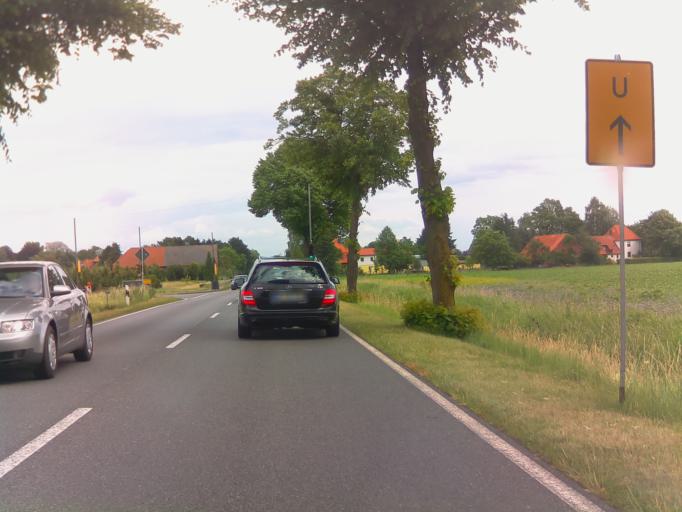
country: DE
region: Lower Saxony
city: Springe
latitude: 52.1736
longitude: 9.6397
